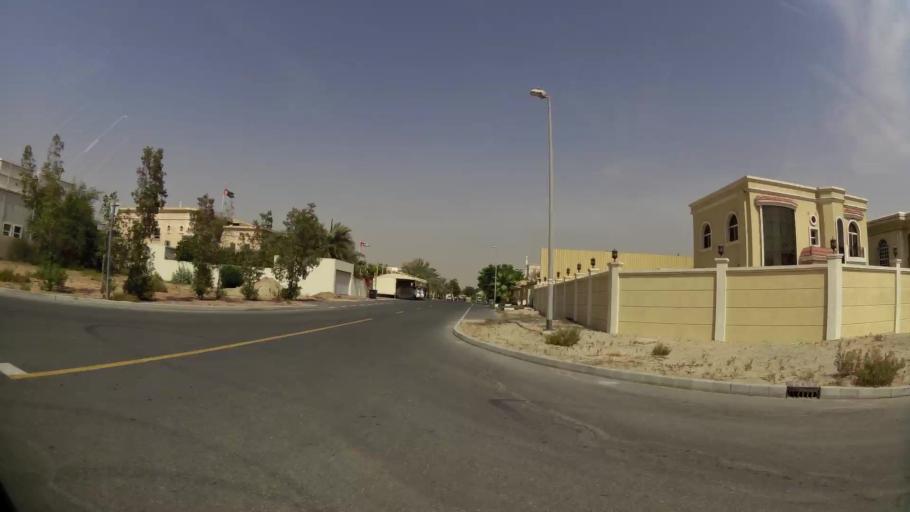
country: AE
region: Ash Shariqah
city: Sharjah
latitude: 25.2468
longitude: 55.4414
